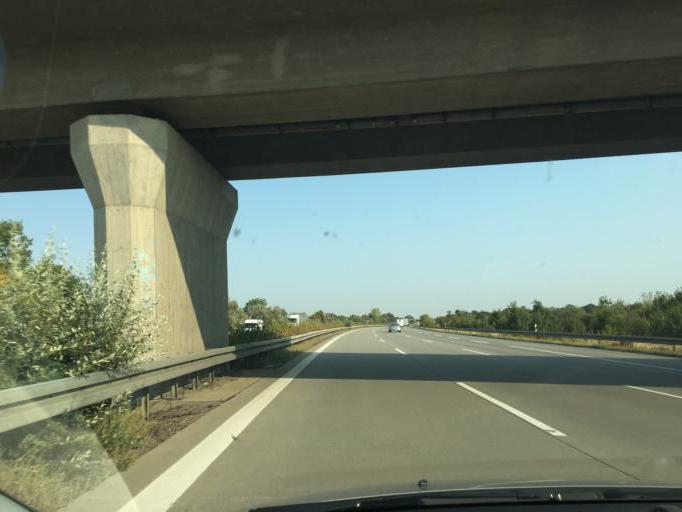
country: DE
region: Saxony
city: Wiedemar
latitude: 51.4936
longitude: 12.2040
